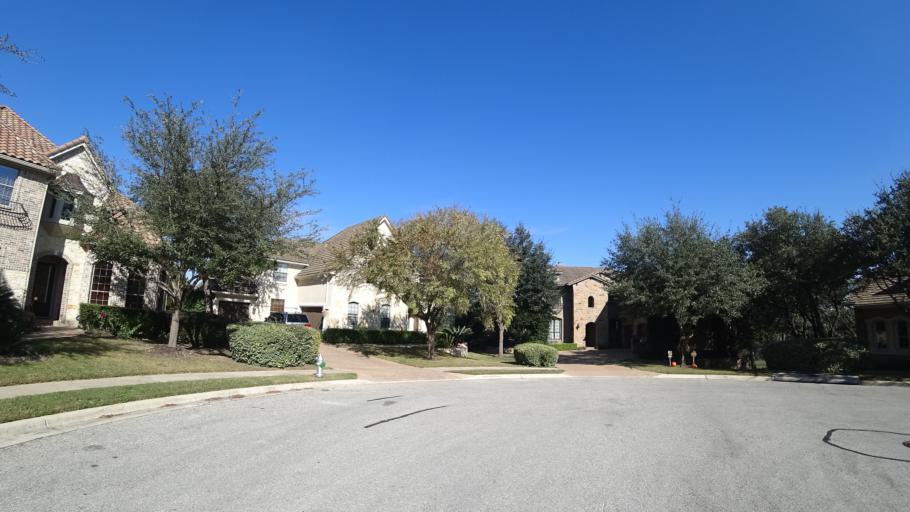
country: US
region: Texas
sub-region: Travis County
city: Barton Creek
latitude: 30.3554
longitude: -97.8874
